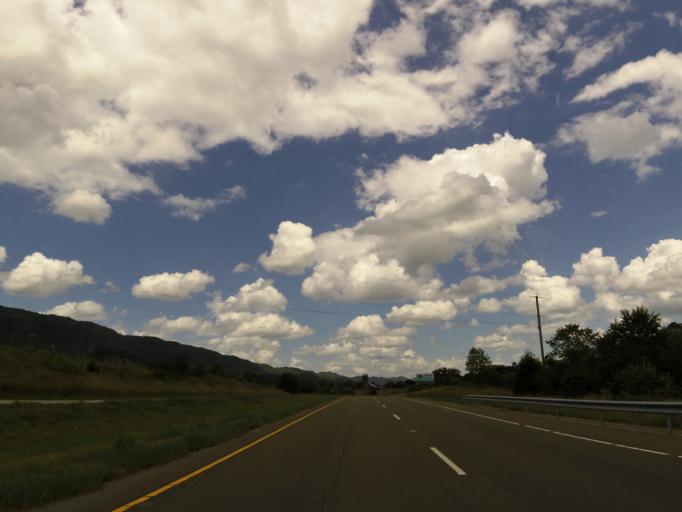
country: US
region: Kentucky
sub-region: Harlan County
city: Loyall
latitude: 36.6429
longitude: -83.4220
